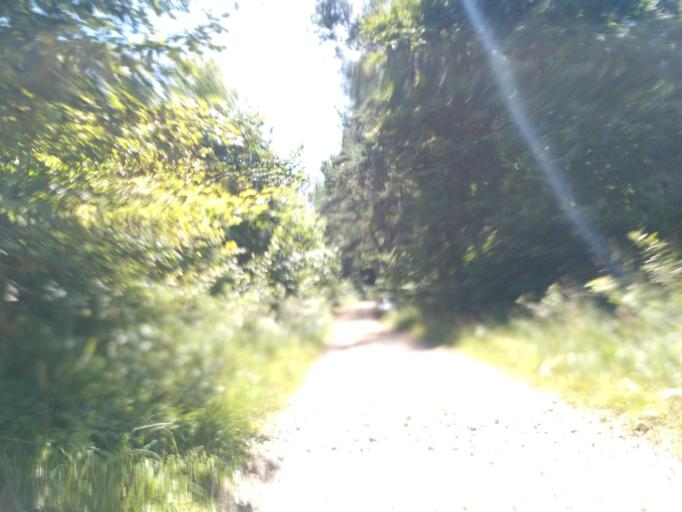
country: PL
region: Subcarpathian Voivodeship
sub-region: Powiat sanocki
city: Bukowsko
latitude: 49.4858
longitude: 22.0935
